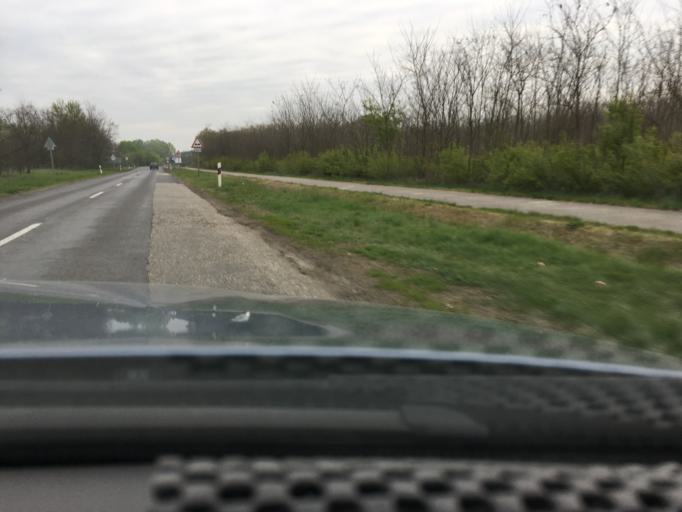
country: HU
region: Hajdu-Bihar
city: Hajdusamson
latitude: 47.6283
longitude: 21.7904
